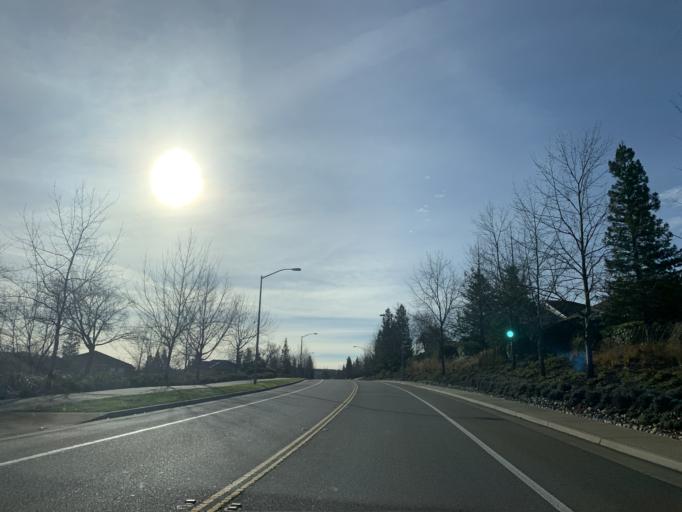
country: US
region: California
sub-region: El Dorado County
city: El Dorado Hills
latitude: 38.6728
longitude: -121.1109
